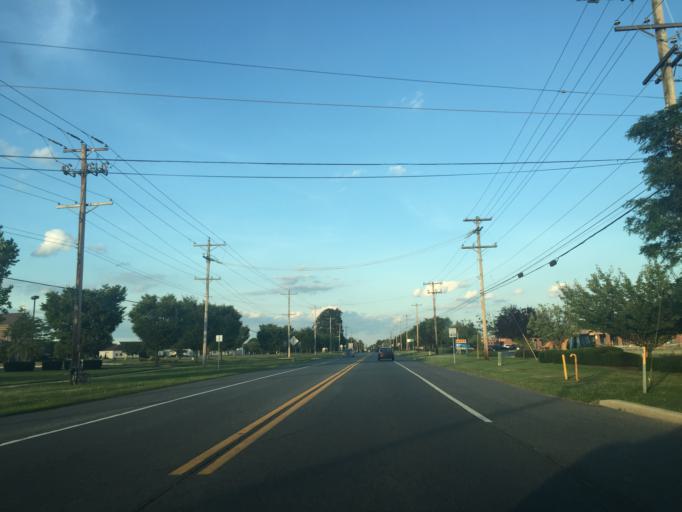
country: US
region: Delaware
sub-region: New Castle County
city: Middletown
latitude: 39.4501
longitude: -75.7075
